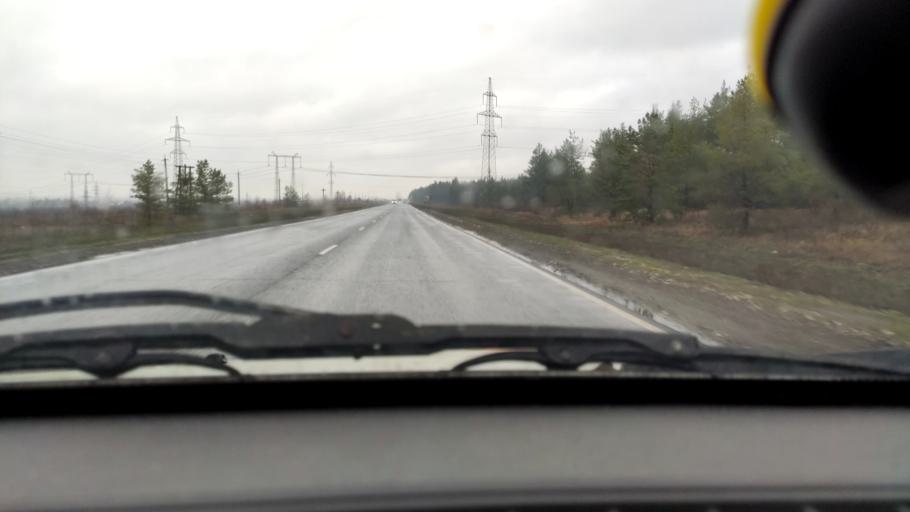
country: RU
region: Samara
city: Zhigulevsk
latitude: 53.5735
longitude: 49.5548
